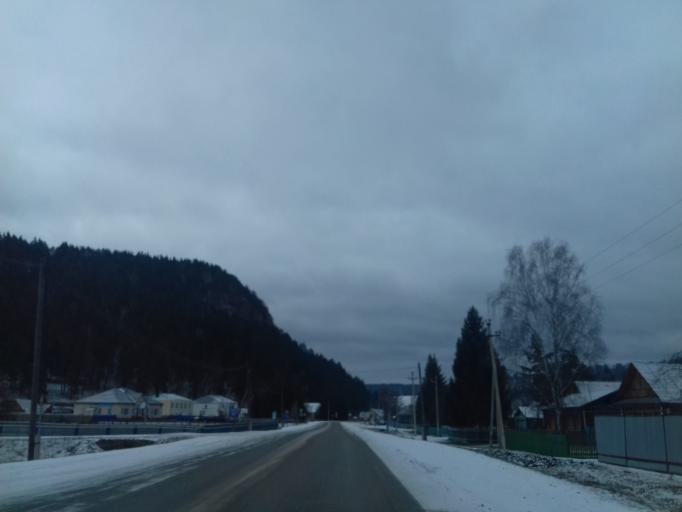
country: RU
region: Bashkortostan
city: Starosubkhangulovo
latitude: 53.1230
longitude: 57.4204
